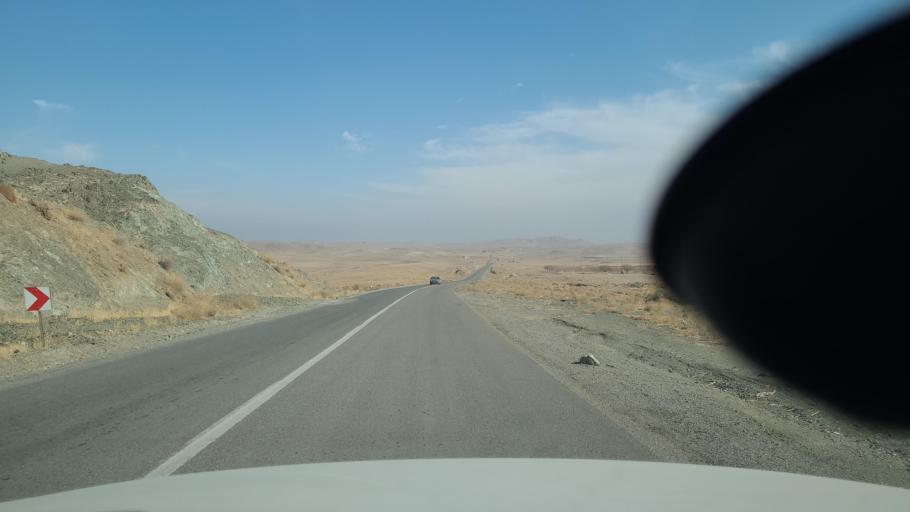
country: IR
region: Razavi Khorasan
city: Fariman
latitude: 35.5949
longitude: 59.7251
